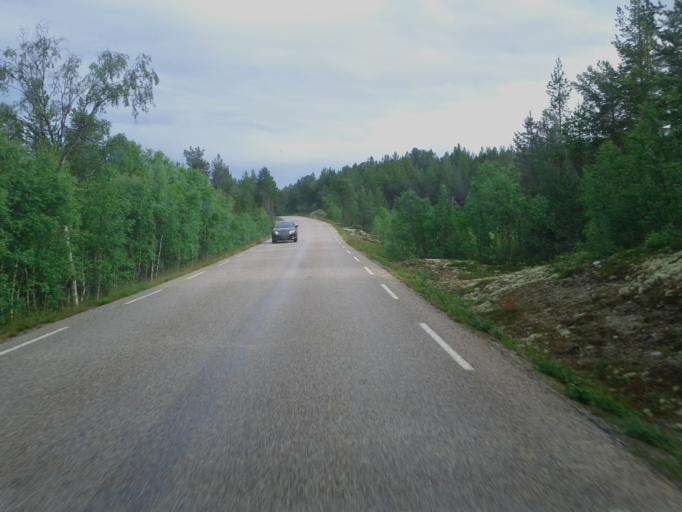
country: NO
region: Hedmark
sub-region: Engerdal
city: Engerdal
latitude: 62.0646
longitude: 11.6789
